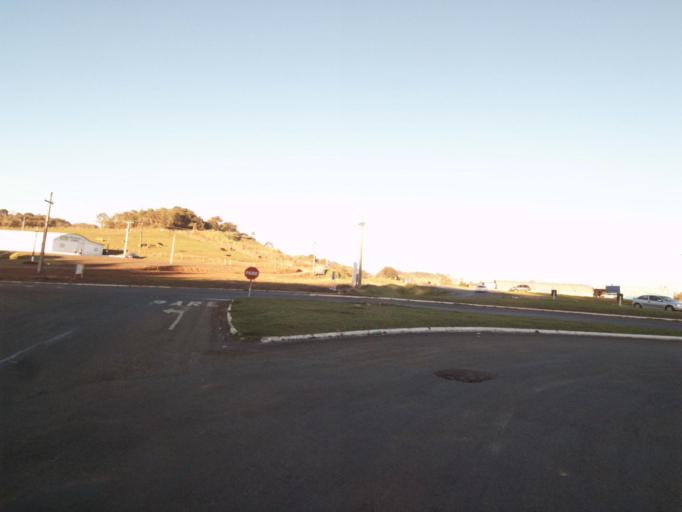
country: BR
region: Santa Catarina
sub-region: Chapeco
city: Chapeco
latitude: -26.8259
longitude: -53.0045
